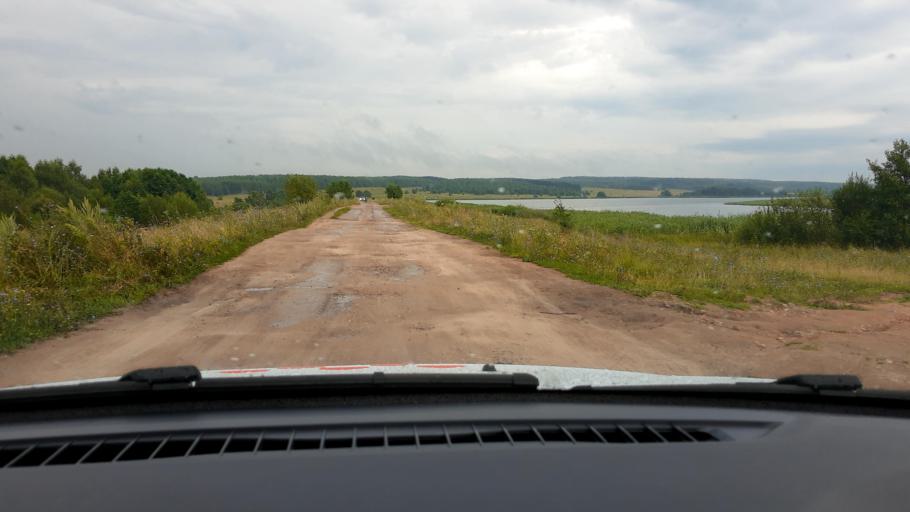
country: RU
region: Nizjnij Novgorod
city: Surovatikha
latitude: 55.9400
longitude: 43.9166
